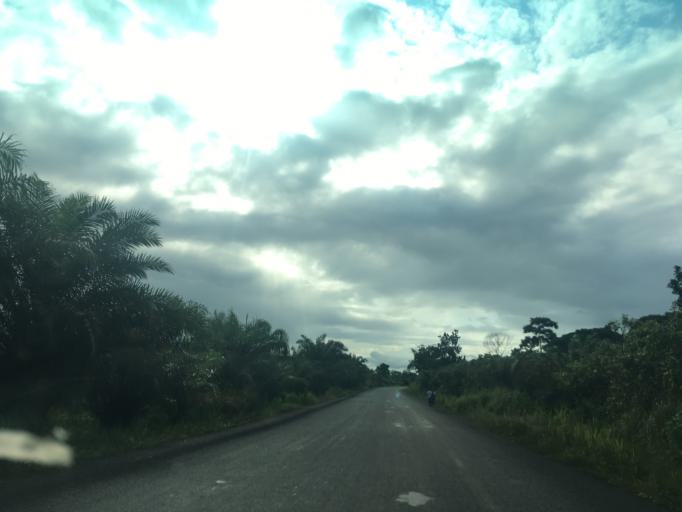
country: GH
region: Western
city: Bibiani
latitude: 6.1212
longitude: -2.3318
